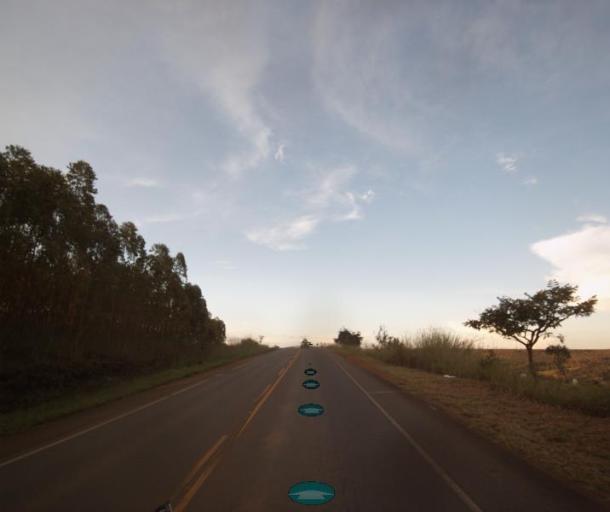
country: BR
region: Goias
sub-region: Abadiania
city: Abadiania
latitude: -16.0928
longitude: -48.8528
